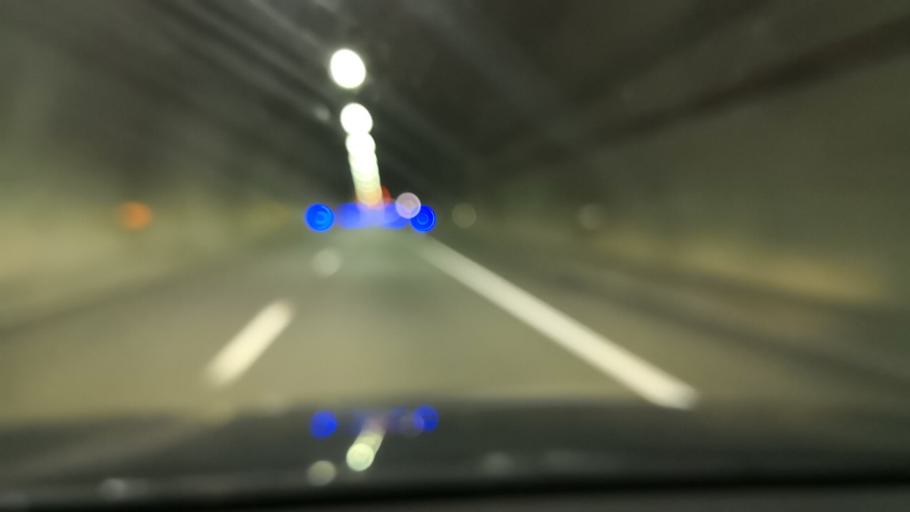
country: PT
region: Vila Real
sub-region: Santa Marta de Penaguiao
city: Santa Marta de Penaguiao
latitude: 41.2749
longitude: -7.8937
